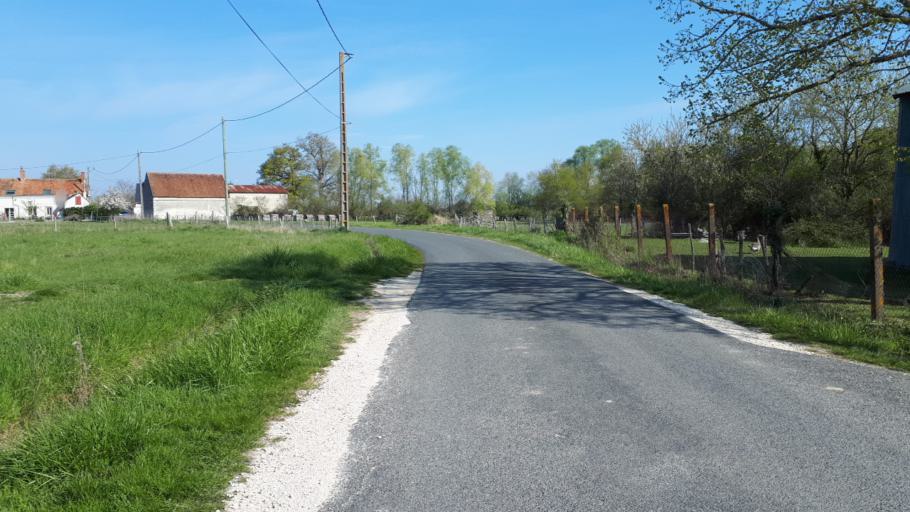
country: FR
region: Centre
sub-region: Departement du Loir-et-Cher
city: Contres
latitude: 47.3797
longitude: 1.3937
